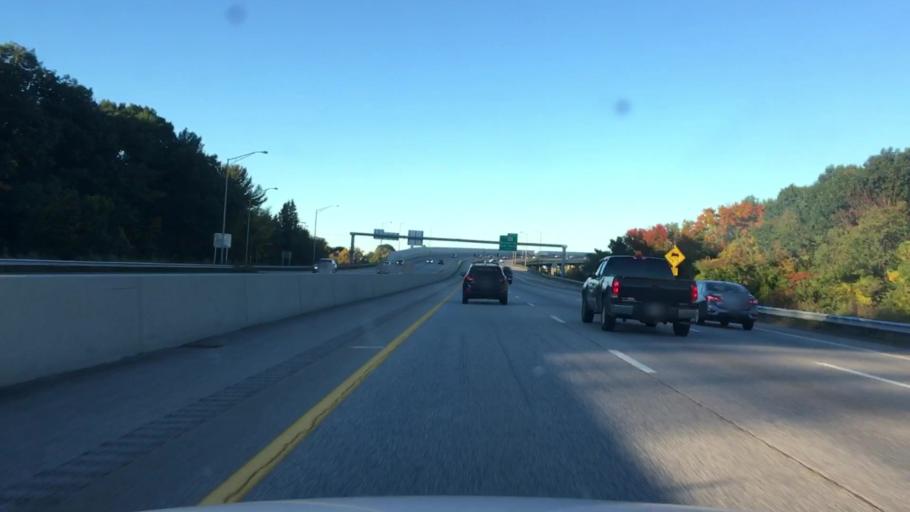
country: US
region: New Hampshire
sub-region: Rockingham County
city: Portsmouth
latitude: 43.0856
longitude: -70.7729
